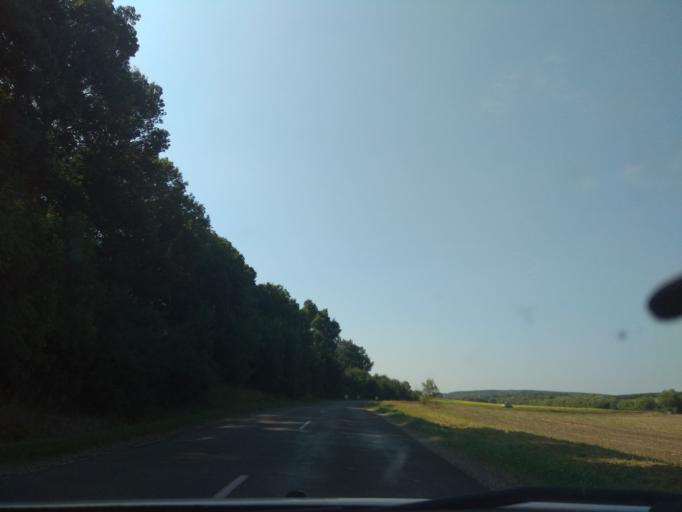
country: HU
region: Borsod-Abauj-Zemplen
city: Harsany
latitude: 47.9414
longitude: 20.7435
